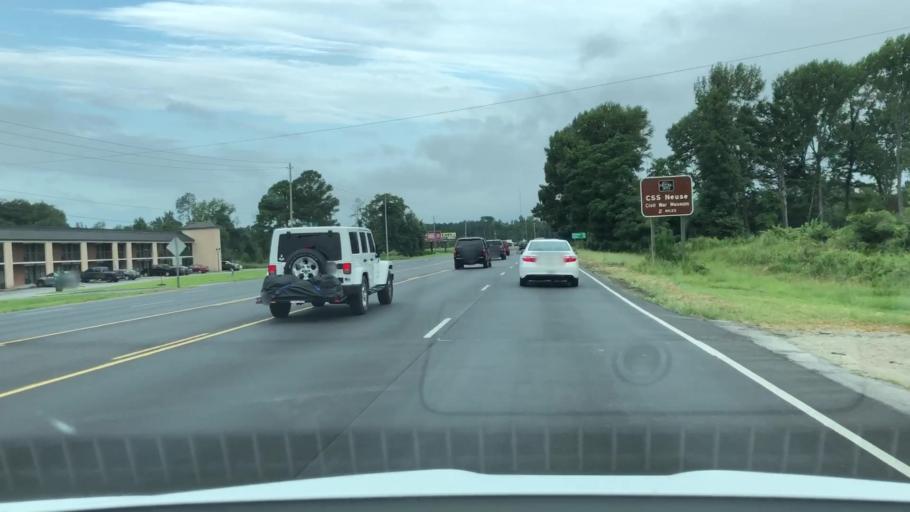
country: US
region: North Carolina
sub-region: Lenoir County
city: Kinston
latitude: 35.2451
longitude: -77.5871
